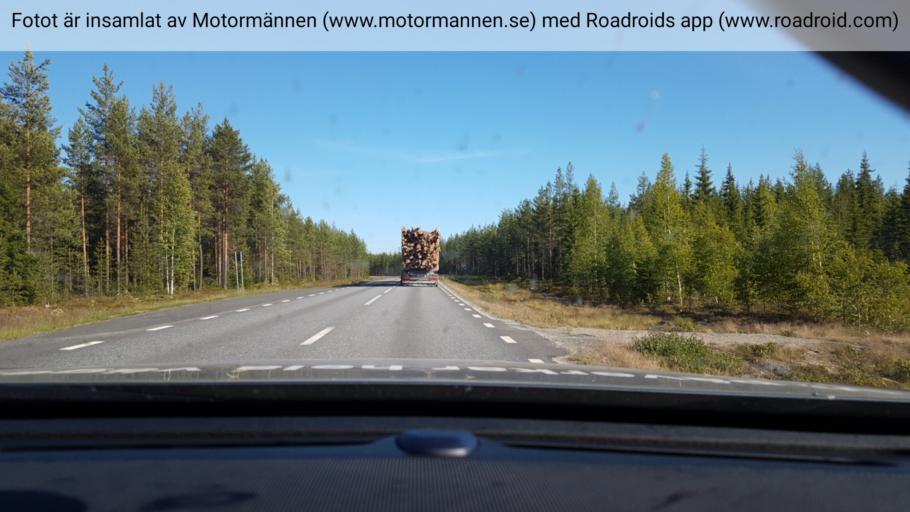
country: SE
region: Vaesterbotten
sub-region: Bjurholms Kommun
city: Bjurholm
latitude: 64.2937
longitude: 19.1841
